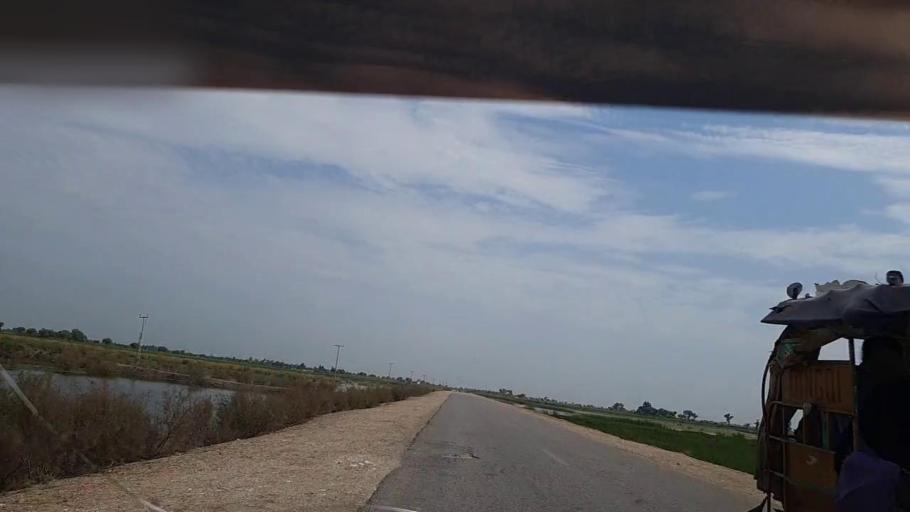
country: PK
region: Sindh
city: Thul
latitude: 28.1979
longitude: 68.7913
